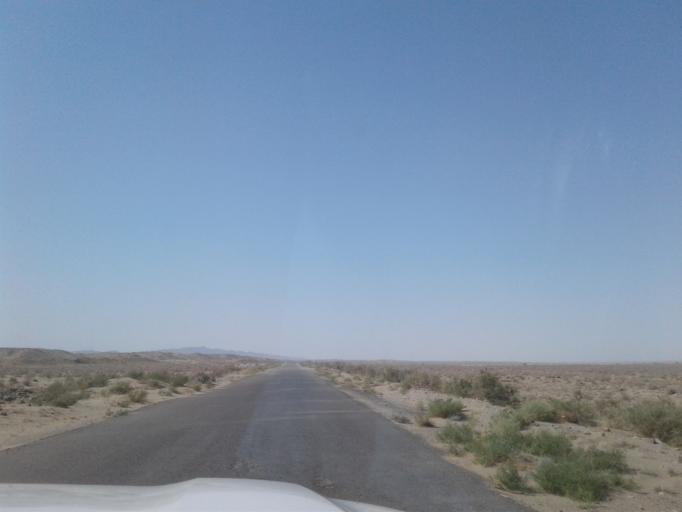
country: TM
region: Balkan
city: Gazanjyk
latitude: 39.2529
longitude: 55.3071
